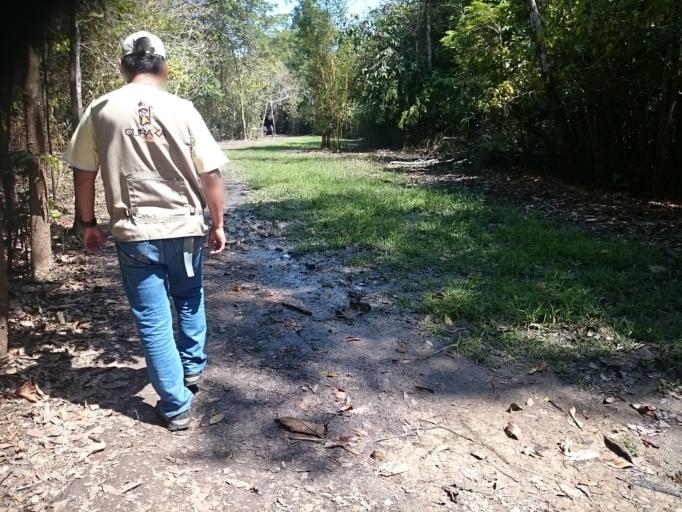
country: PE
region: Loreto
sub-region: Provincia de Maynas
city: Iquitos
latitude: -3.6853
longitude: -73.2818
